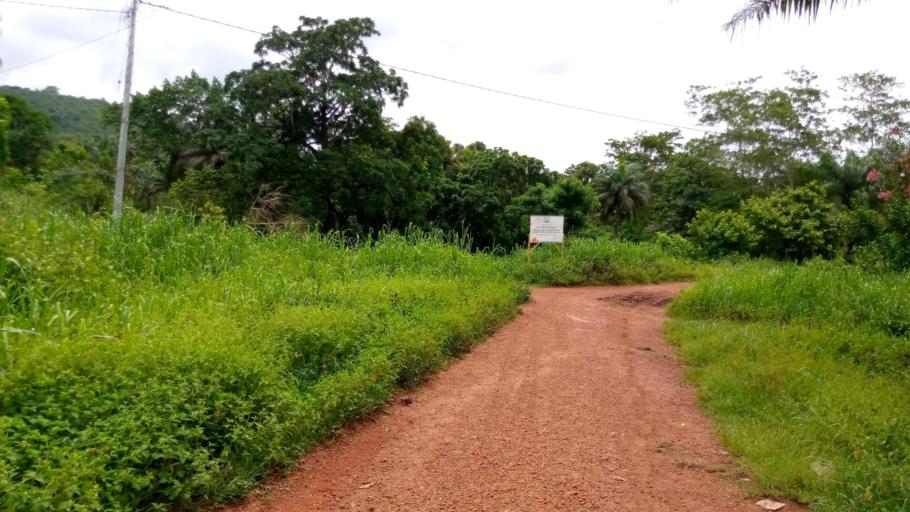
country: SL
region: Southern Province
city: Rotifunk
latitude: 8.1895
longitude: -12.5740
